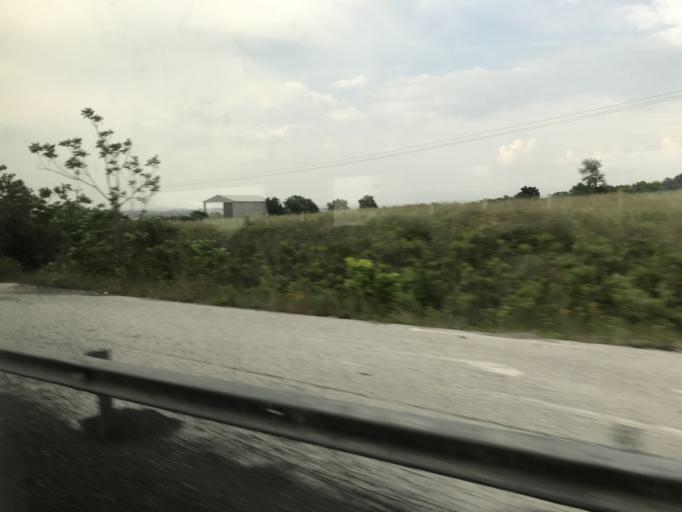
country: GR
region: East Macedonia and Thrace
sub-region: Nomos Rodopis
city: Sapes
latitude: 40.9568
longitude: 25.6501
